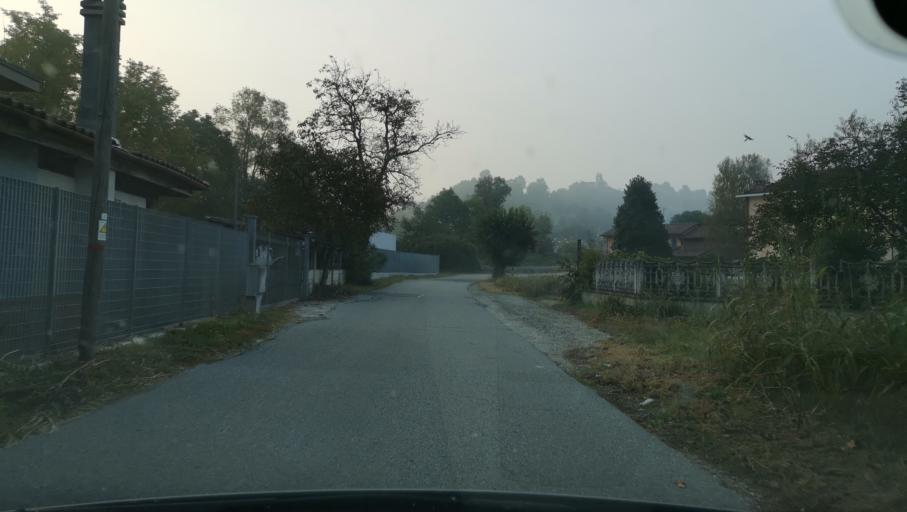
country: IT
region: Piedmont
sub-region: Provincia di Torino
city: Castiglione Torinese
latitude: 45.1248
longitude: 7.8120
